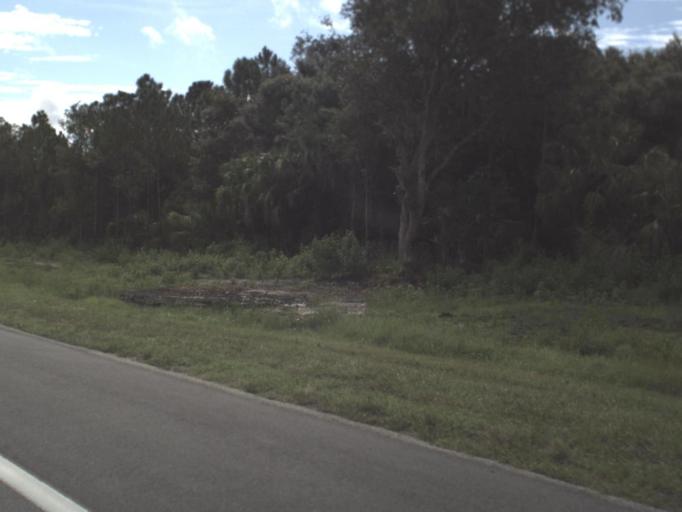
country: US
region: Florida
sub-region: Sarasota County
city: Plantation
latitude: 27.1118
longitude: -82.3320
